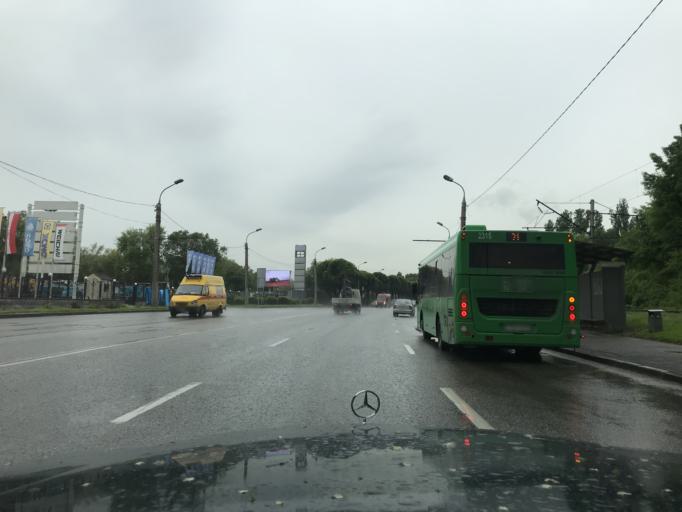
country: KZ
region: Almaty Qalasy
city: Almaty
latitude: 43.2998
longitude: 76.9511
